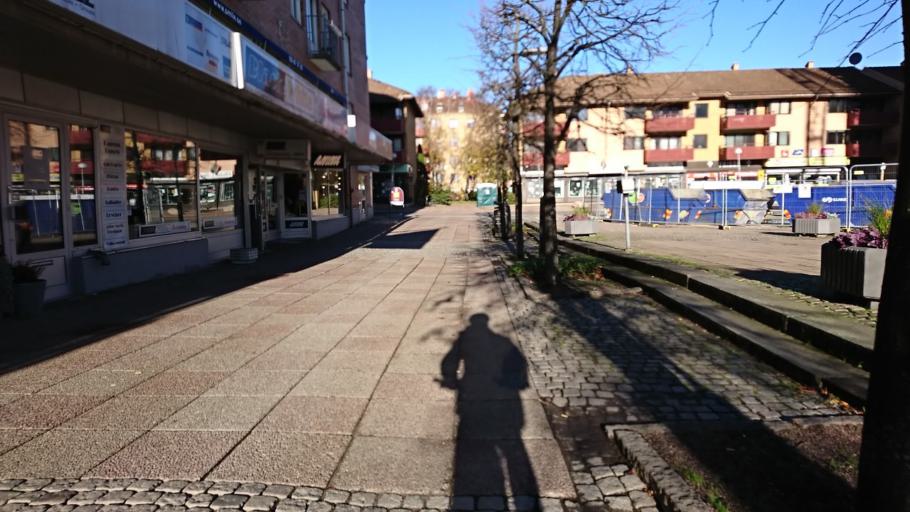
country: SE
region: Vaestra Goetaland
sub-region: Molndal
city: Moelndal
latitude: 57.6557
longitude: 12.0149
